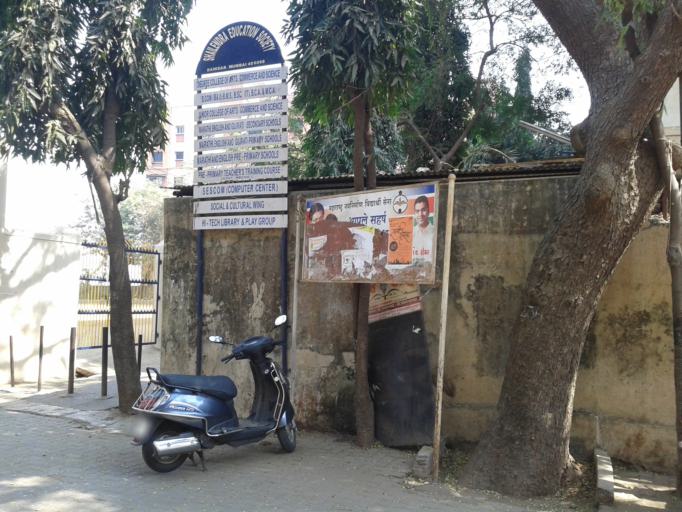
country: IN
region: Maharashtra
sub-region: Mumbai Suburban
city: Borivli
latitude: 19.2460
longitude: 72.8635
